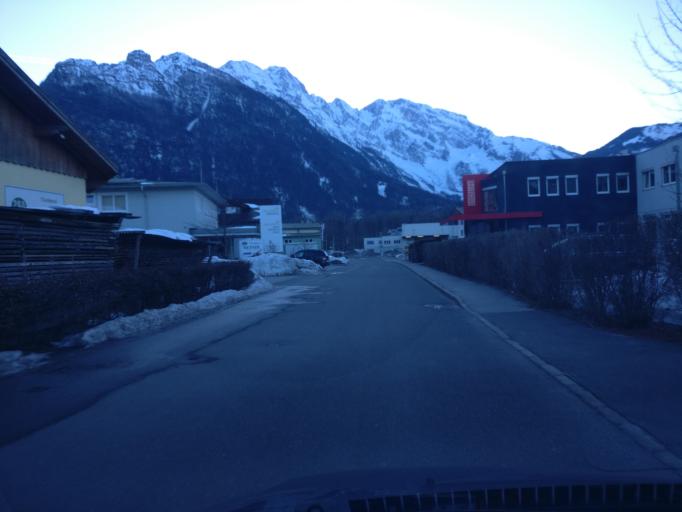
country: AT
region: Salzburg
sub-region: Politischer Bezirk Hallein
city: Golling an der Salzach
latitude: 47.6081
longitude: 13.1646
